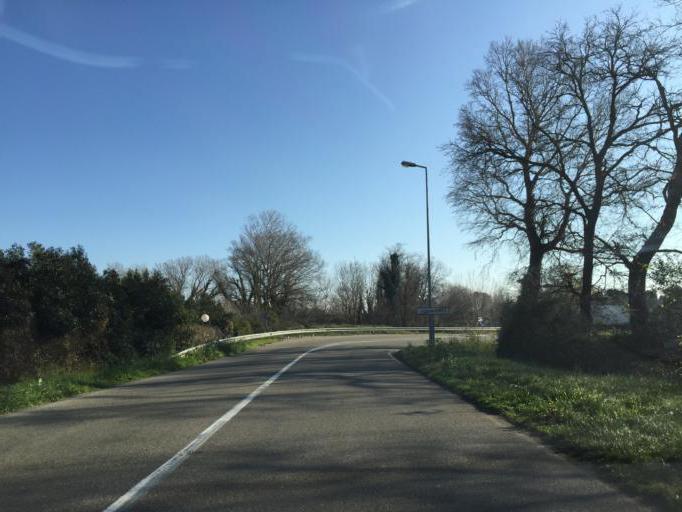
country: FR
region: Provence-Alpes-Cote d'Azur
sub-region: Departement du Vaucluse
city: Jonquieres
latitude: 44.1082
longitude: 4.9159
